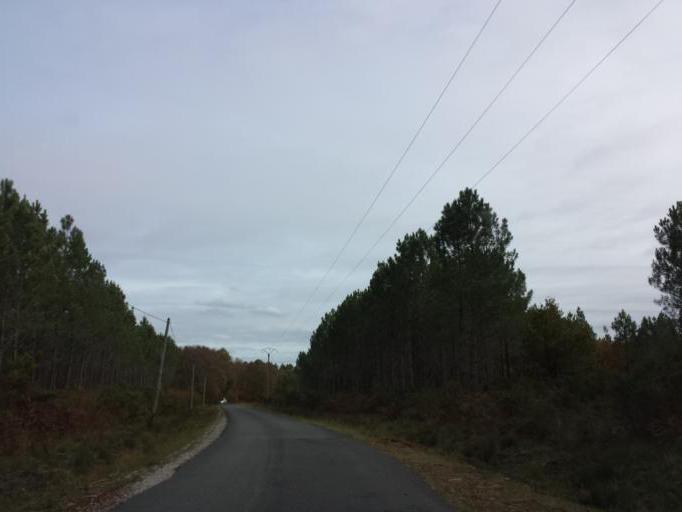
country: FR
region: Aquitaine
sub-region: Departement de la Gironde
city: Lacanau
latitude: 44.9475
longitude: -1.0617
